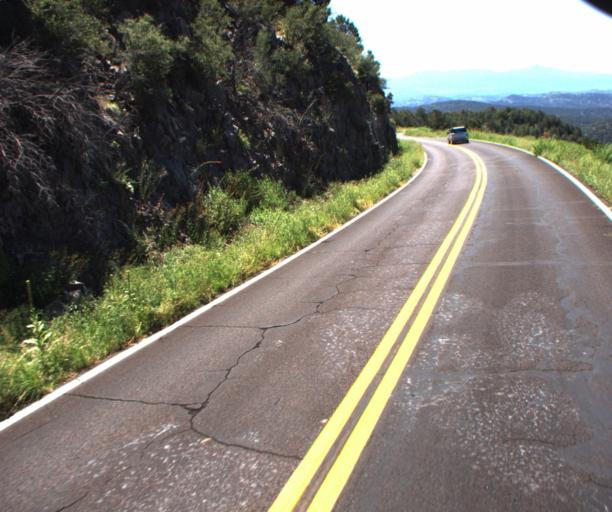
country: US
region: Arizona
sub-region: Greenlee County
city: Morenci
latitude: 33.4308
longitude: -109.3767
